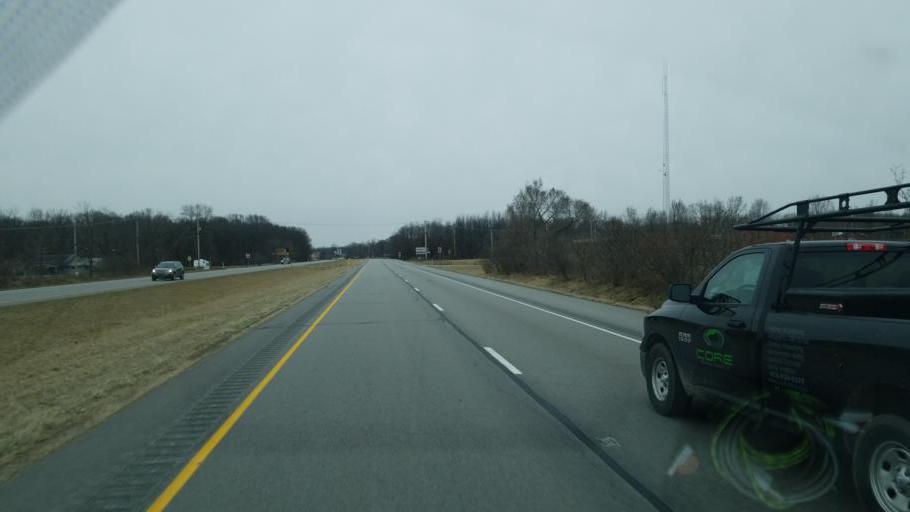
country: US
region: Indiana
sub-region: Marshall County
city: Plymouth
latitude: 41.3048
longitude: -86.2753
